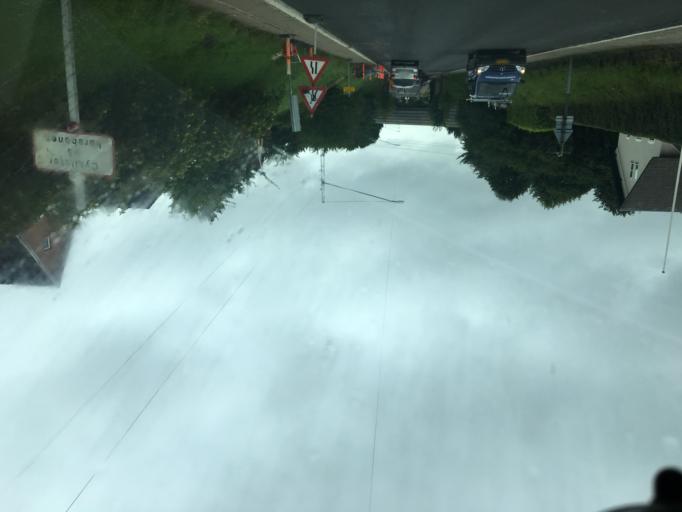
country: DK
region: South Denmark
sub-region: Middelfart Kommune
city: Middelfart
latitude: 55.4950
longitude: 9.7526
